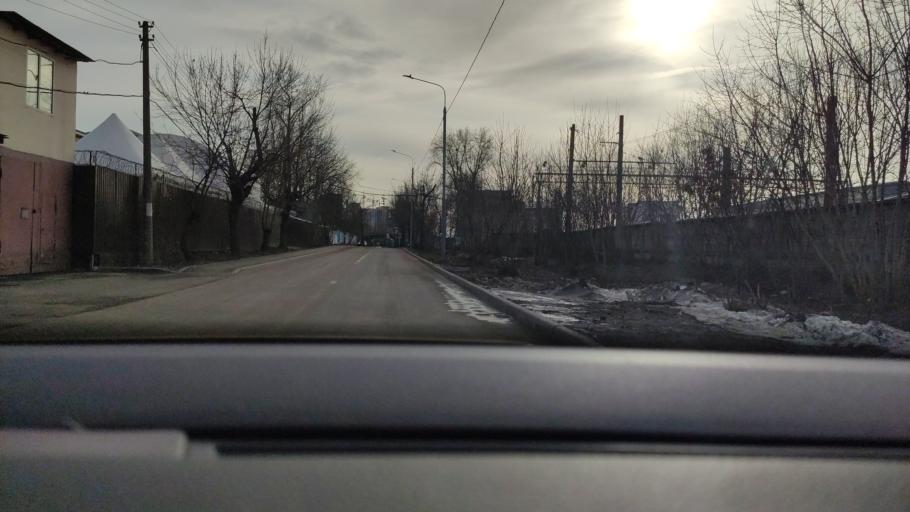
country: RU
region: Moscow
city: Lyublino
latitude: 55.6737
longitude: 37.7325
